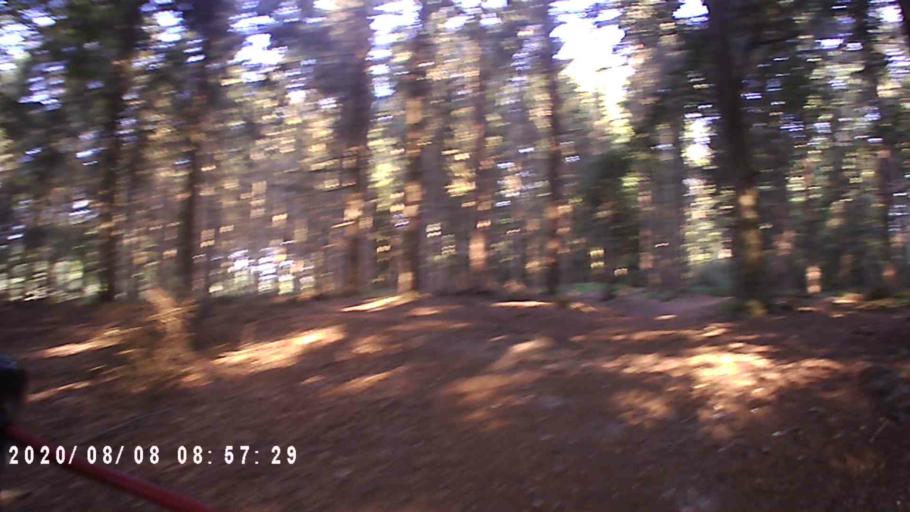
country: NL
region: Groningen
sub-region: Gemeente Leek
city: Leek
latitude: 53.0538
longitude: 6.3228
